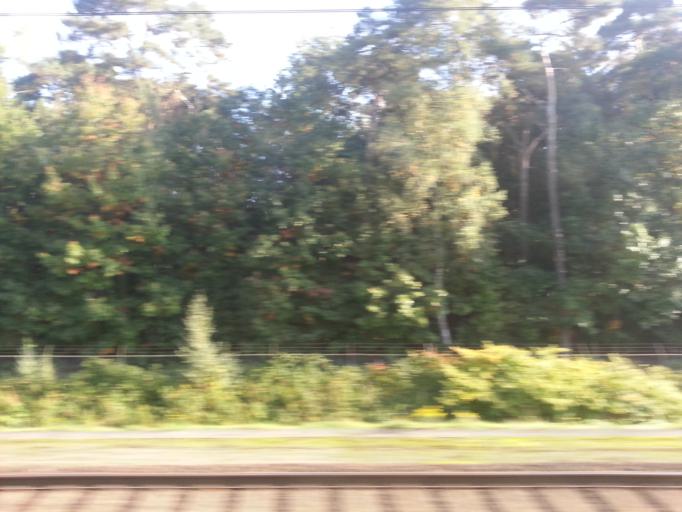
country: NL
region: North Brabant
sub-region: Gemeente Eindhoven
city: Meerhoven
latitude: 51.4630
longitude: 5.4403
